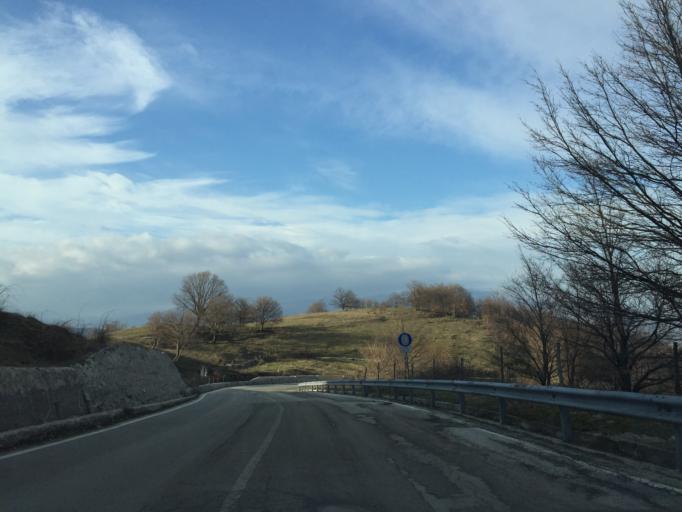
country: IT
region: Molise
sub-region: Provincia di Campobasso
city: San Massimo
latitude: 41.4786
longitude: 14.4073
